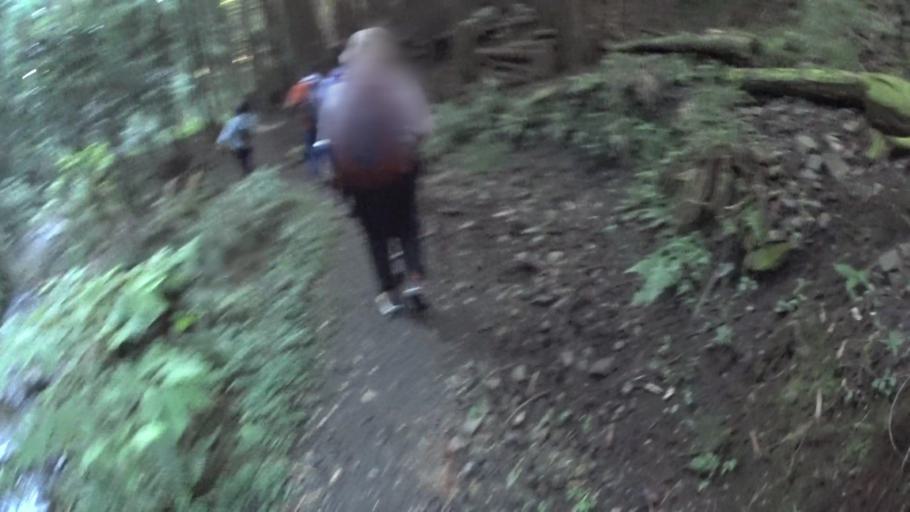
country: JP
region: Shiga Prefecture
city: Kitahama
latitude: 35.1092
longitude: 135.8305
